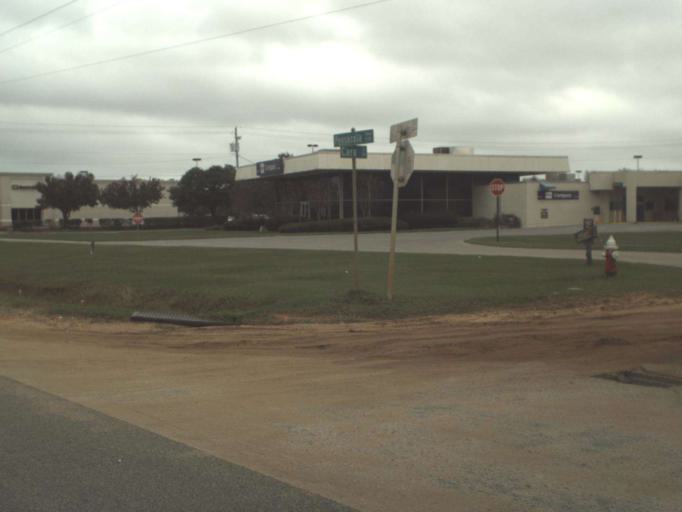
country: US
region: Florida
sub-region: Escambia County
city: Ensley
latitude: 30.5254
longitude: -87.2744
